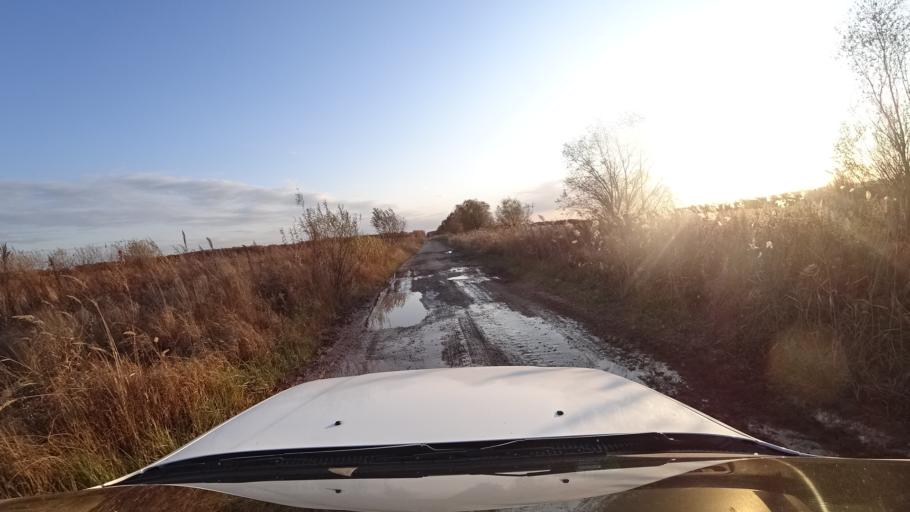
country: RU
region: Primorskiy
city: Lazo
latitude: 45.8113
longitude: 133.6083
